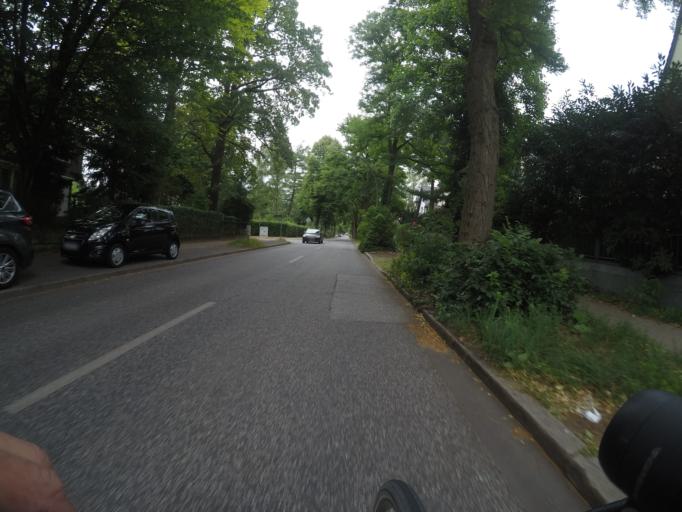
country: DE
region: Hamburg
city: Marienthal
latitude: 53.5649
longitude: 10.0699
